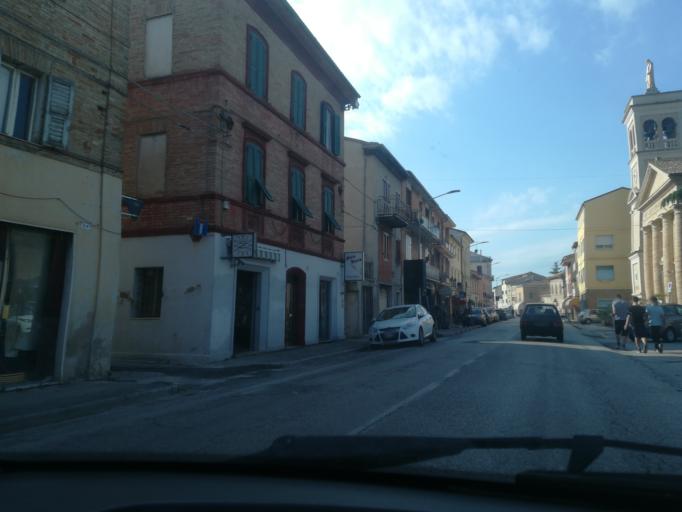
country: IT
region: The Marches
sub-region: Provincia di Macerata
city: Villa Potenza
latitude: 43.3219
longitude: 13.4267
